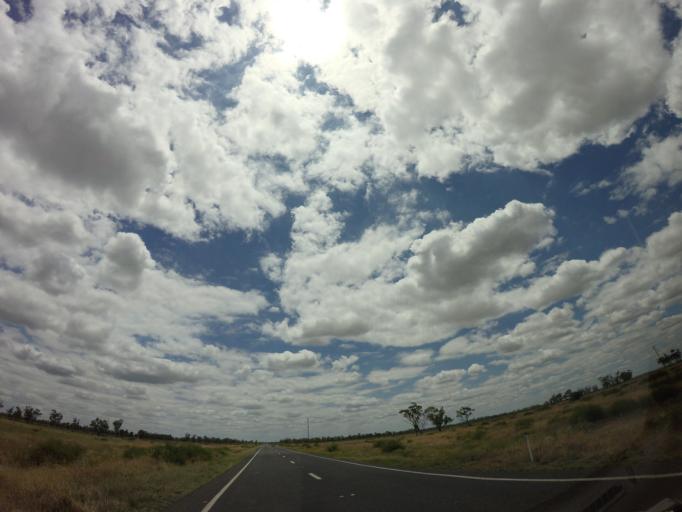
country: AU
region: New South Wales
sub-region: Moree Plains
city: Boggabilla
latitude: -28.6666
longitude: 150.3208
